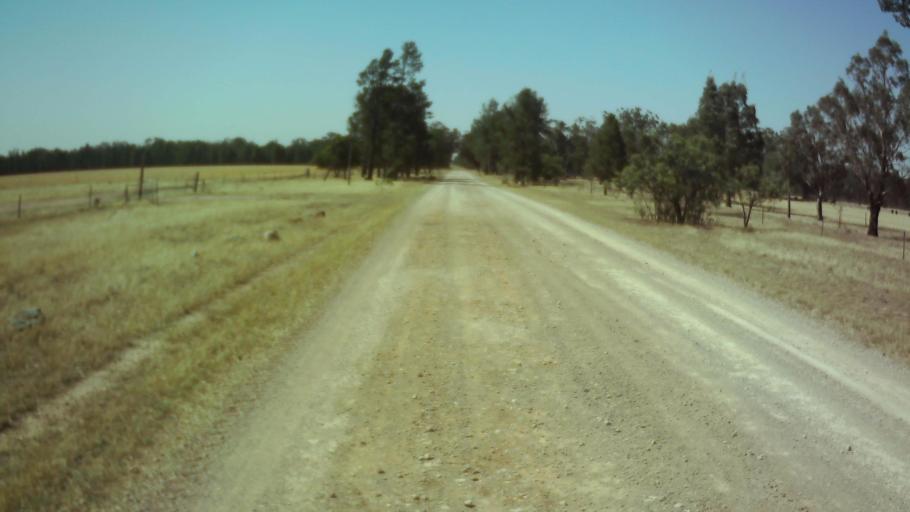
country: AU
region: New South Wales
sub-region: Weddin
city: Grenfell
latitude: -33.9793
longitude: 147.9287
